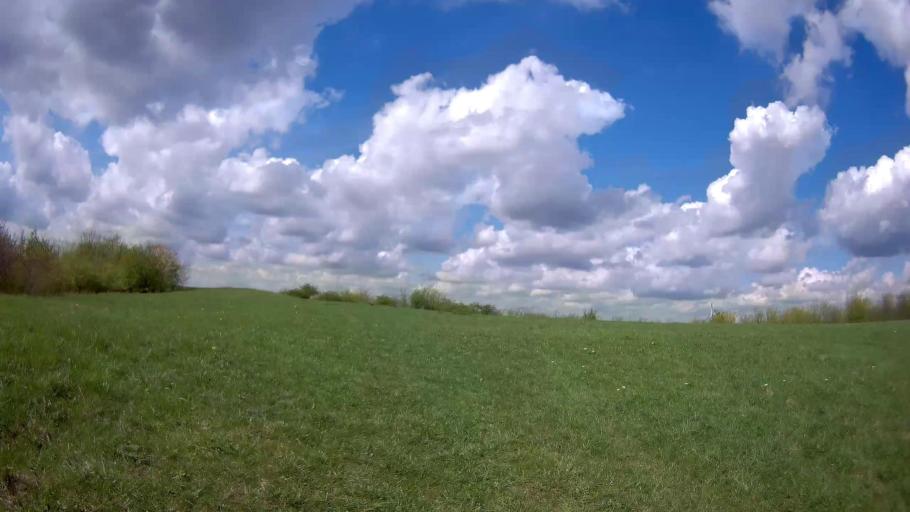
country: DE
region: North Rhine-Westphalia
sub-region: Regierungsbezirk Munster
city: Gladbeck
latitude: 51.5652
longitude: 7.0349
